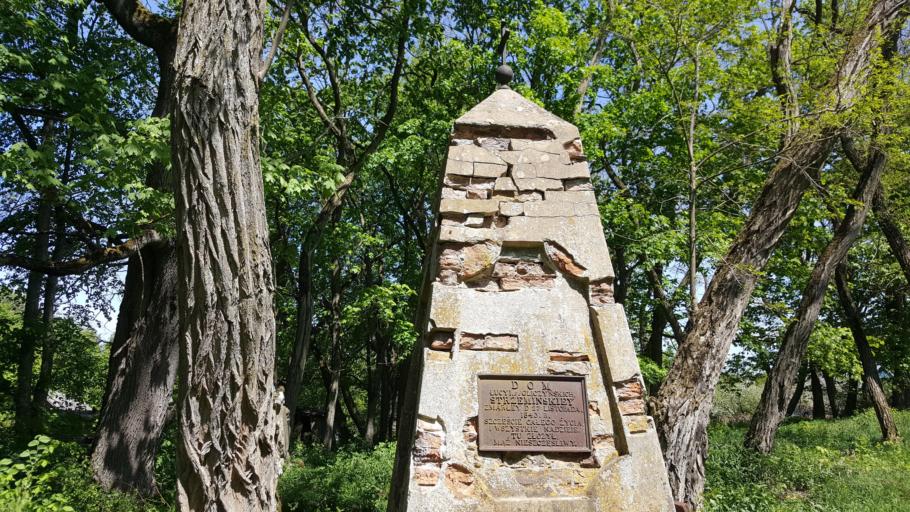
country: BY
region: Brest
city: Zhabinka
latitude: 52.3543
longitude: 24.1542
